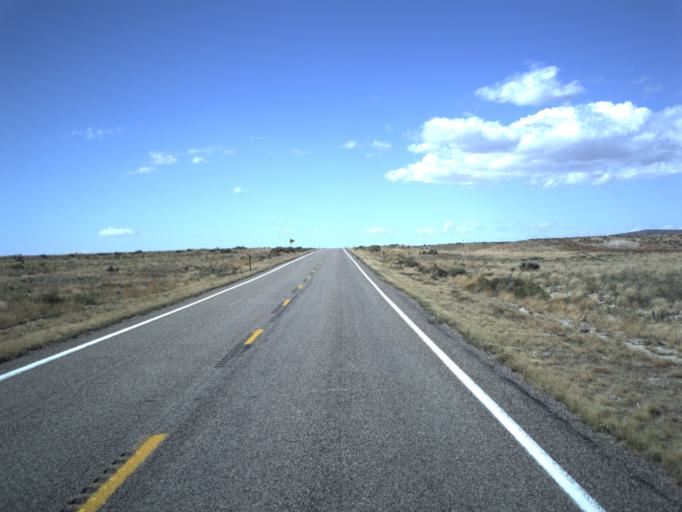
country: US
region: Utah
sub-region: Beaver County
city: Milford
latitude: 38.8108
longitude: -112.8715
